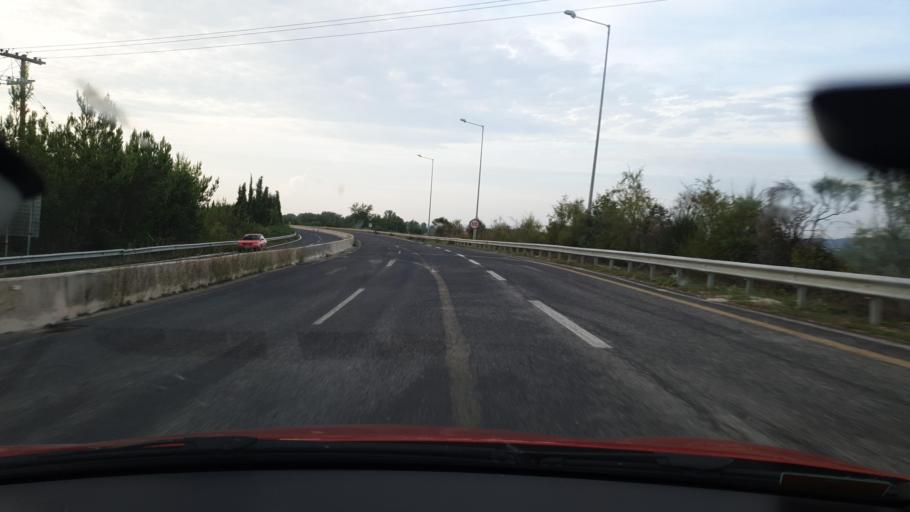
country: GR
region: Central Macedonia
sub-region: Nomos Kilkis
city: Nea Santa
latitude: 40.8505
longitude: 22.9020
